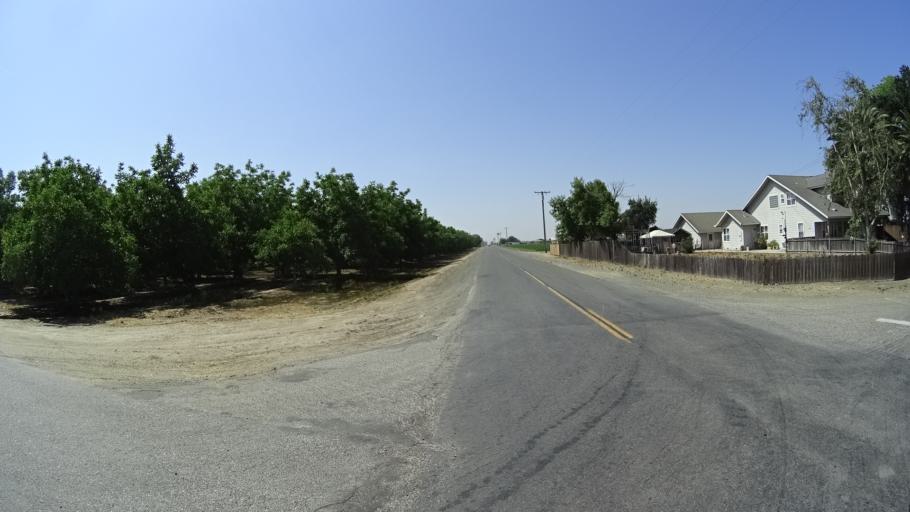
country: US
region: California
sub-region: Kings County
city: Hanford
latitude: 36.3721
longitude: -119.5469
